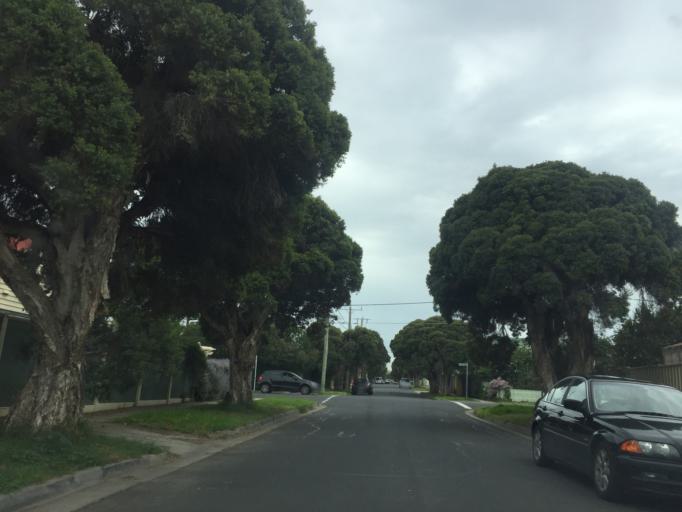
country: AU
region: Victoria
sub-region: Darebin
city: Preston
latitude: -37.7367
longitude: 145.0099
